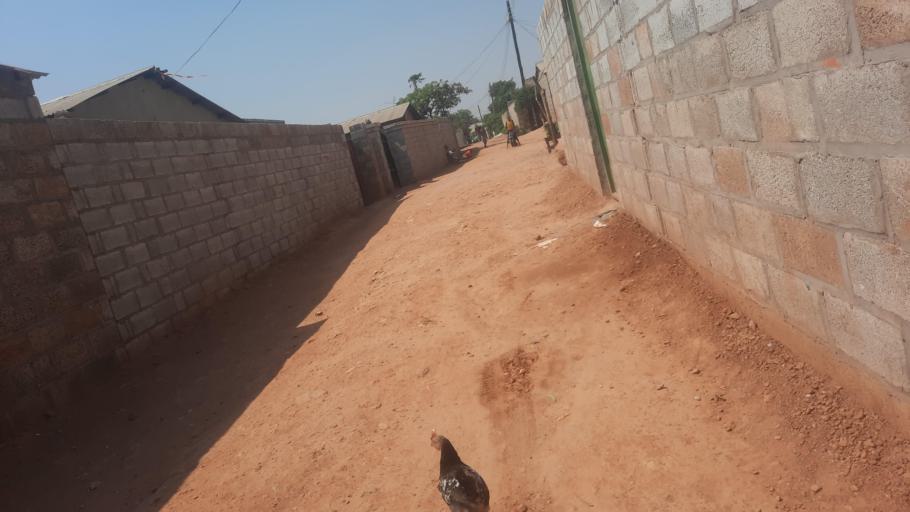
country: ZM
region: Lusaka
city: Lusaka
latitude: -15.3967
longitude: 28.3760
